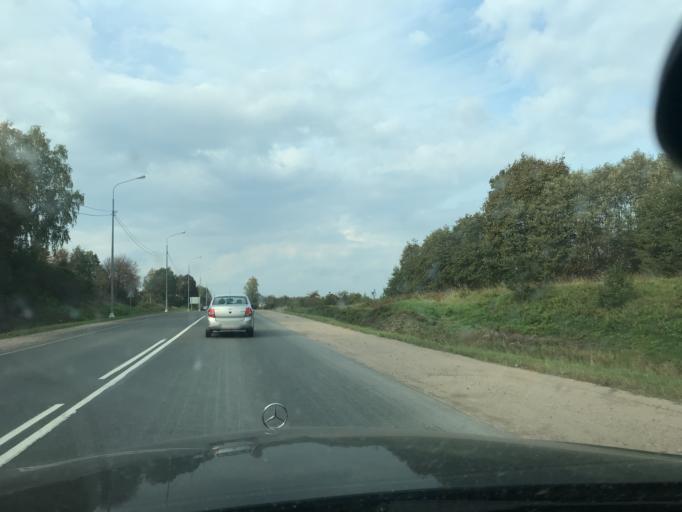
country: RU
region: Pskov
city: Ostrov
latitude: 57.3042
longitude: 28.3698
